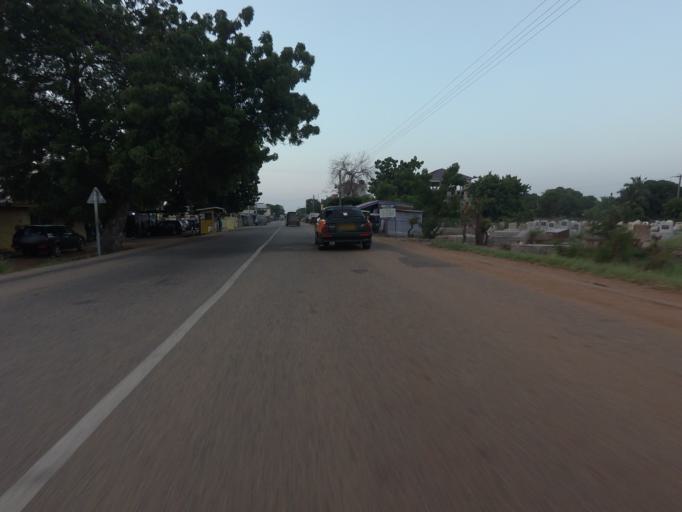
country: GH
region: Volta
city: Keta
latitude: 5.8784
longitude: 0.9816
